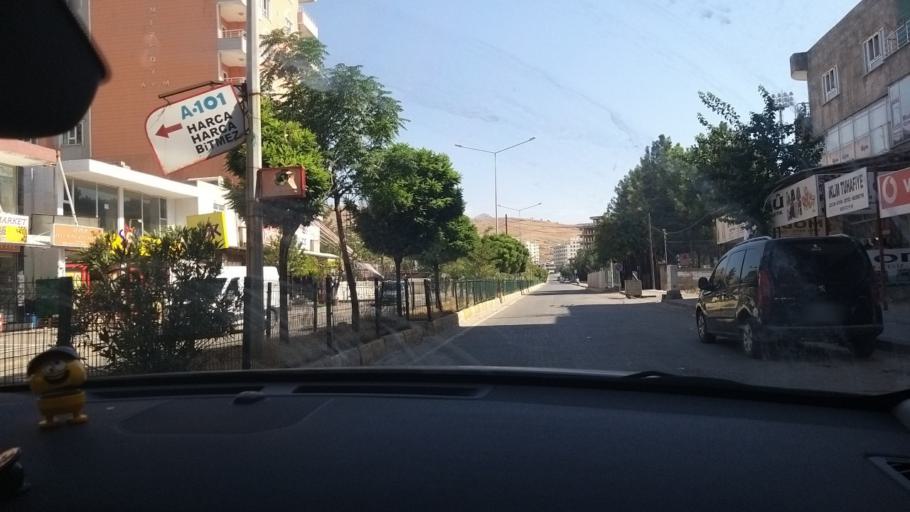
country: TR
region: Batman
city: Kozluk
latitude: 38.1676
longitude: 41.5015
